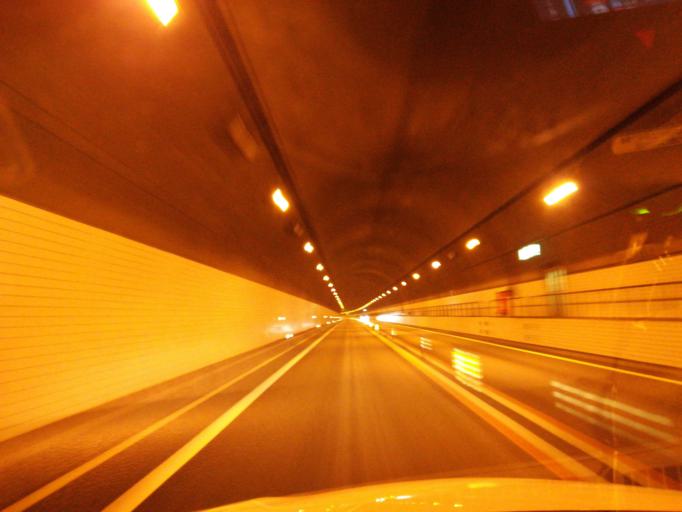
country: JP
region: Tokushima
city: Ikedacho
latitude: 34.0214
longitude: 133.8022
